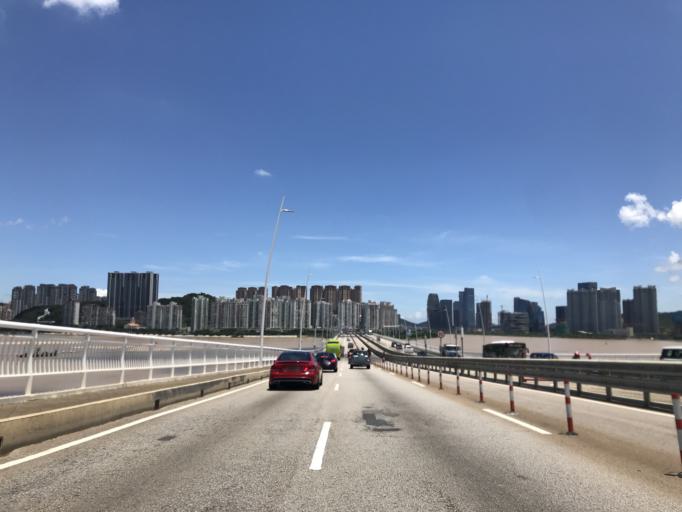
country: MO
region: Macau
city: Macau
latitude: 22.1724
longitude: 113.5363
